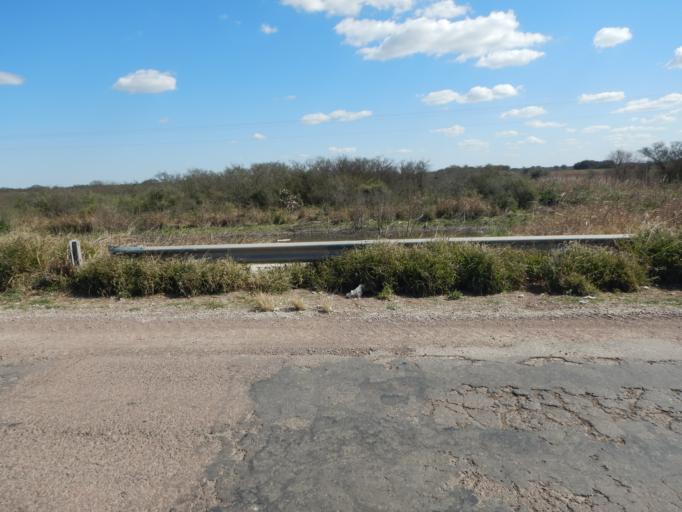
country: AR
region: Santiago del Estero
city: Los Juries
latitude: -28.6512
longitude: -61.5268
